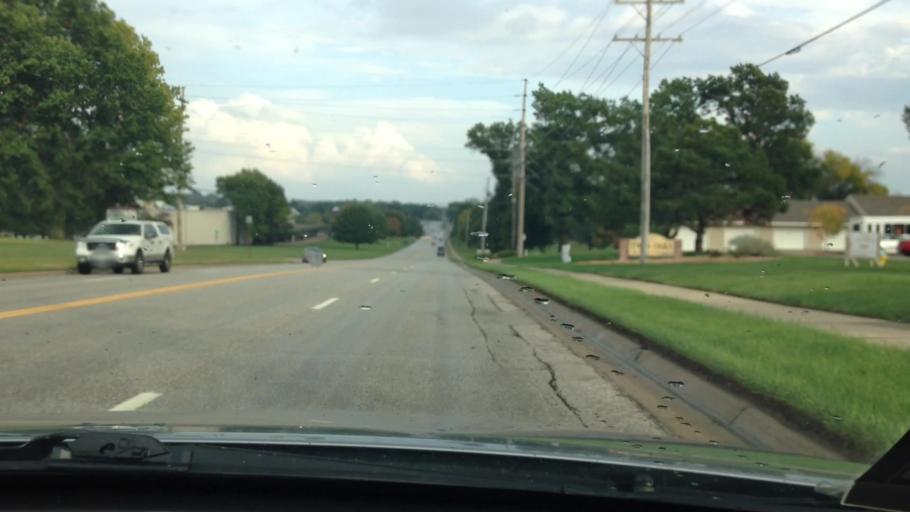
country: US
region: Kansas
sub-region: Leavenworth County
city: Lansing
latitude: 39.2668
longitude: -94.9105
